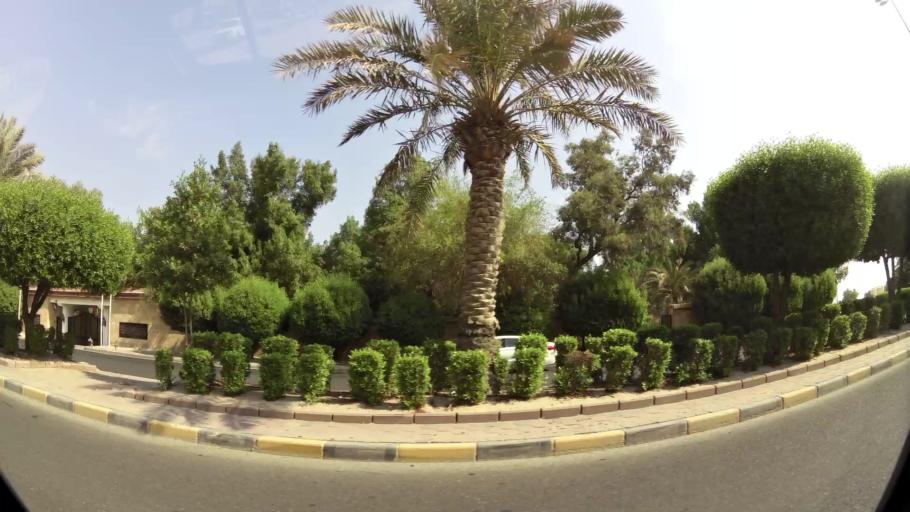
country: KW
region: Al Ahmadi
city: Al Mahbulah
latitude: 29.1466
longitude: 48.1280
